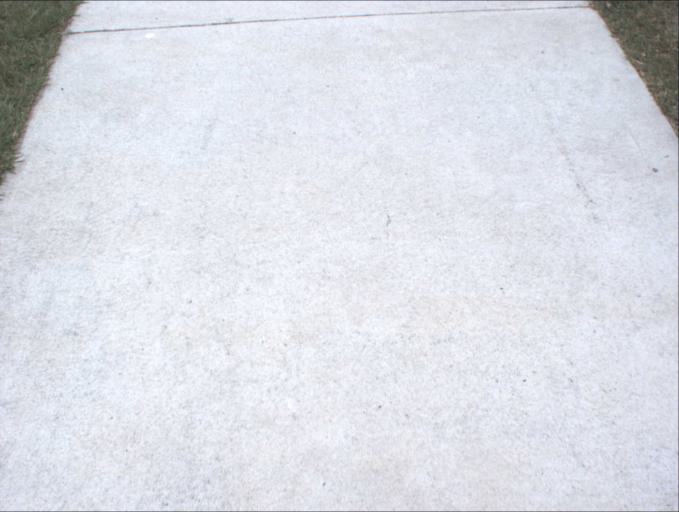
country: AU
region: Queensland
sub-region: Logan
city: Beenleigh
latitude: -27.7113
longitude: 153.1914
